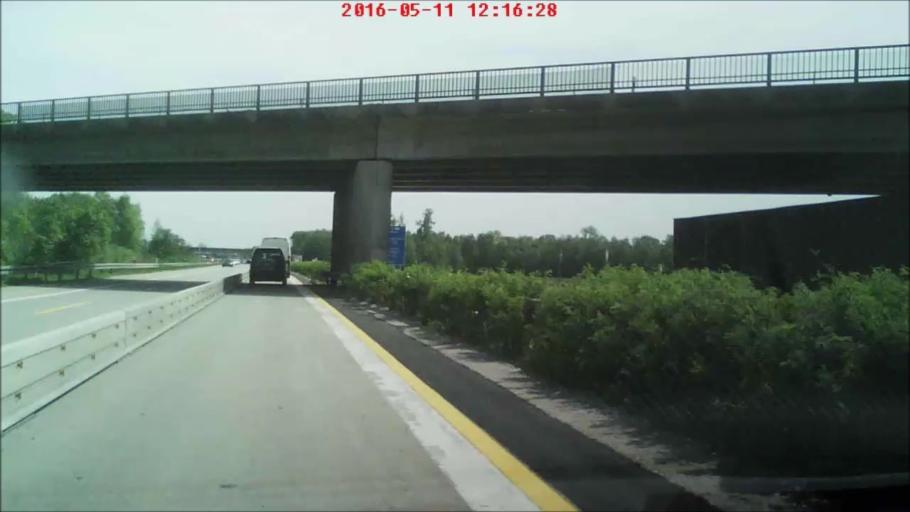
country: DE
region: Bavaria
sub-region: Lower Bavaria
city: Metten
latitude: 48.8236
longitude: 12.9258
